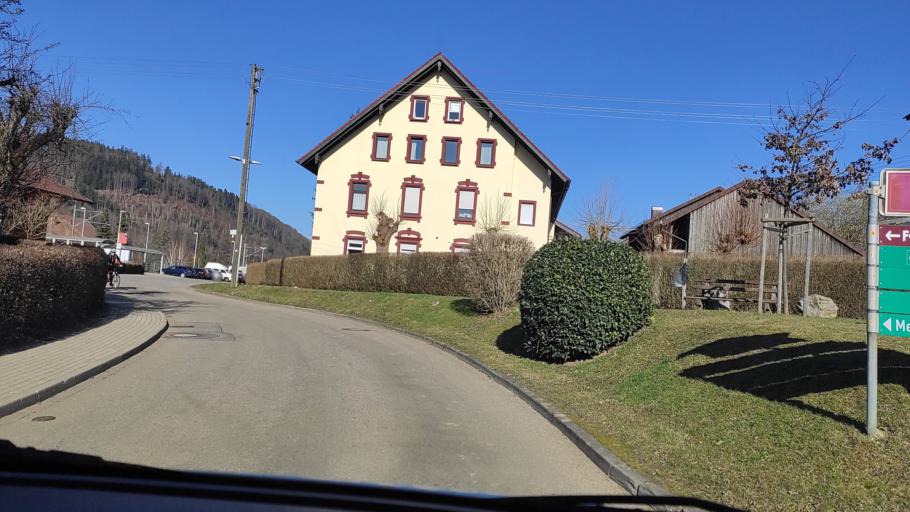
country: DE
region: Baden-Wuerttemberg
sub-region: Freiburg Region
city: Elzach
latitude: 48.1519
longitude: 8.0448
